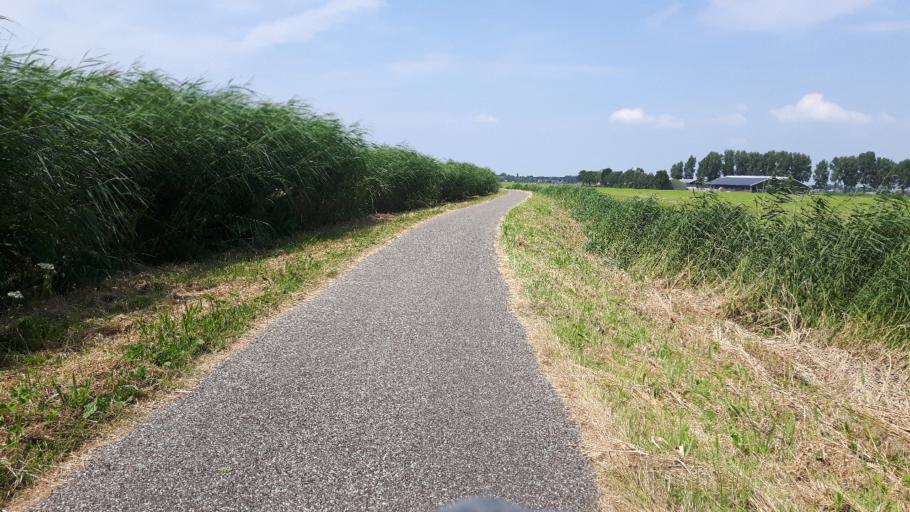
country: NL
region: South Holland
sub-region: Molenwaard
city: Liesveld
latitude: 51.9080
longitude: 4.8357
